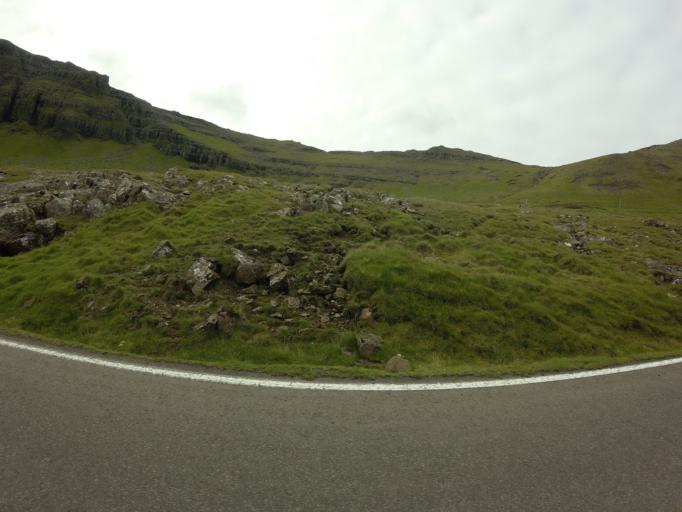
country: FO
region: Suduroy
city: Tvoroyri
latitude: 61.5726
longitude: -6.9334
